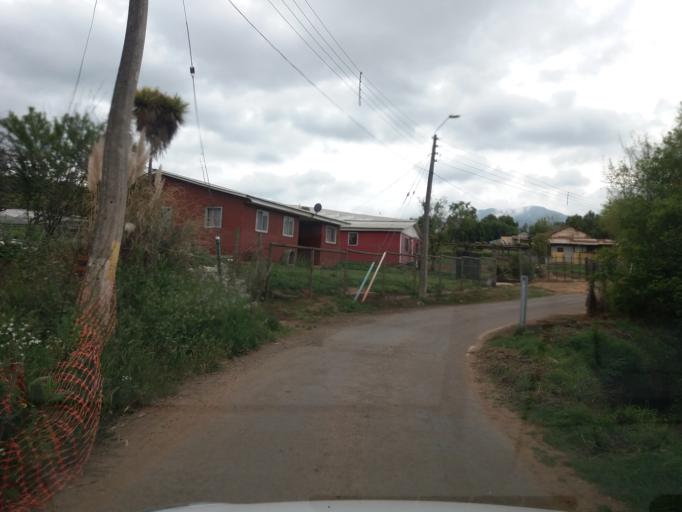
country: CL
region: Valparaiso
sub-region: Provincia de Quillota
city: Quillota
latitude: -32.8937
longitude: -71.3209
